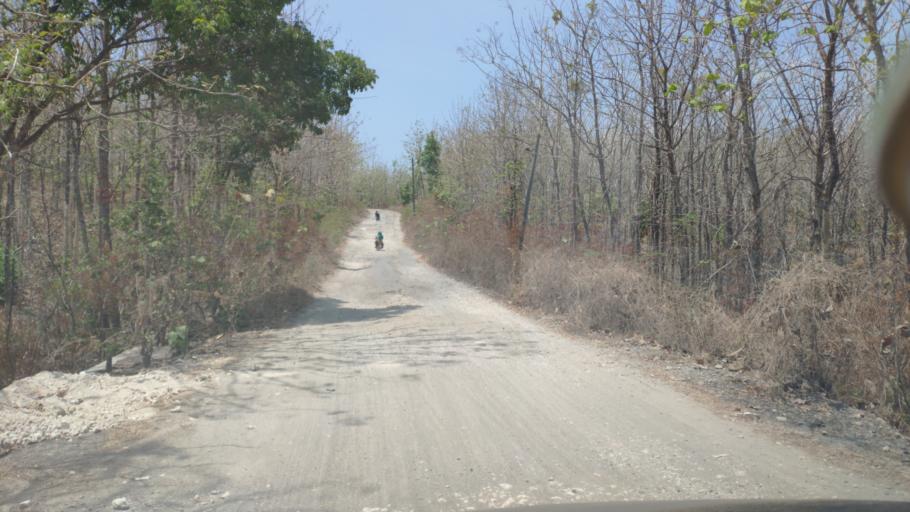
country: ID
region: Central Java
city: Randublatung
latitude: -7.2496
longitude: 111.3786
